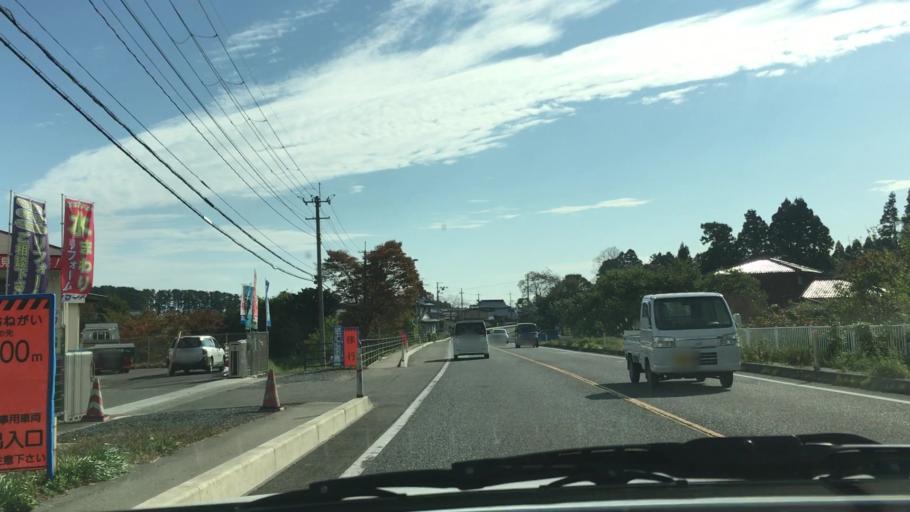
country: JP
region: Aomori
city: Hachinohe
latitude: 40.4269
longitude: 141.6942
